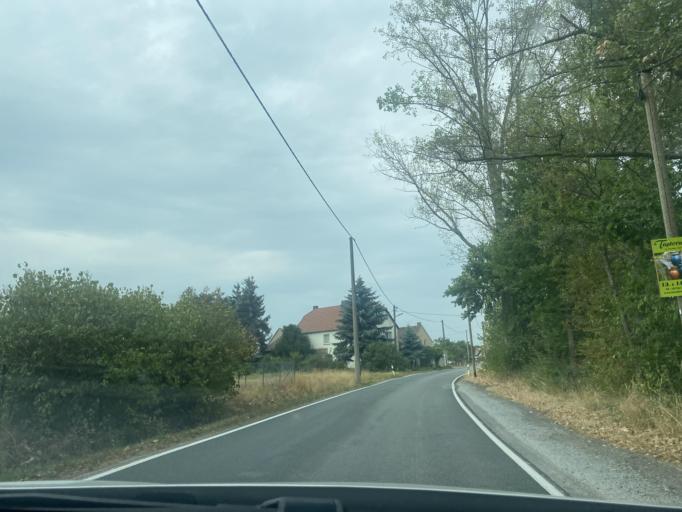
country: DE
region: Saxony
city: Konigswartha
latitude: 51.3355
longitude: 14.2960
